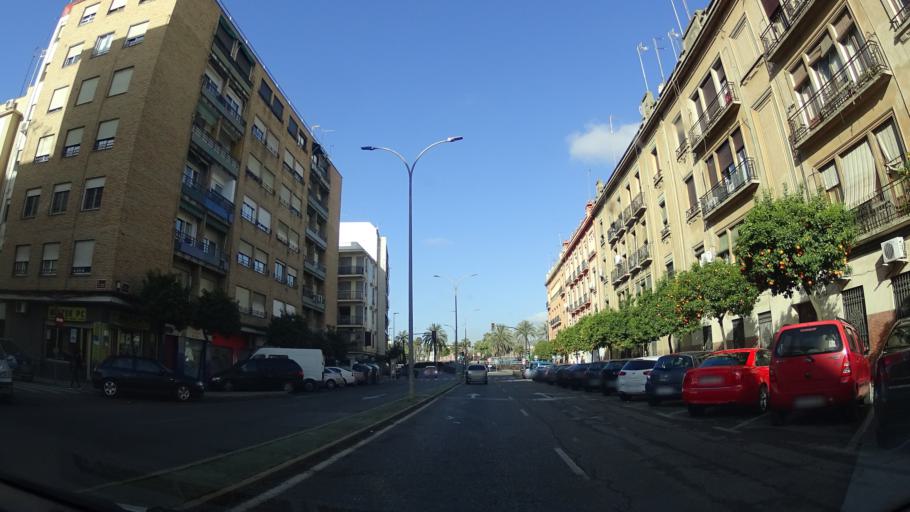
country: ES
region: Andalusia
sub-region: Province of Cordoba
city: Cordoba
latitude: 37.8854
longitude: -4.7931
